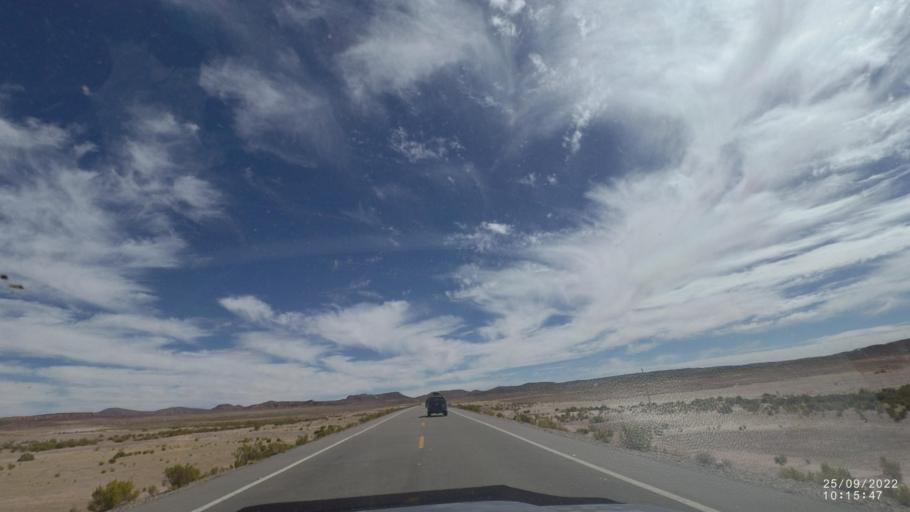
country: BO
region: Potosi
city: Colchani
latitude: -20.0419
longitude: -66.8699
